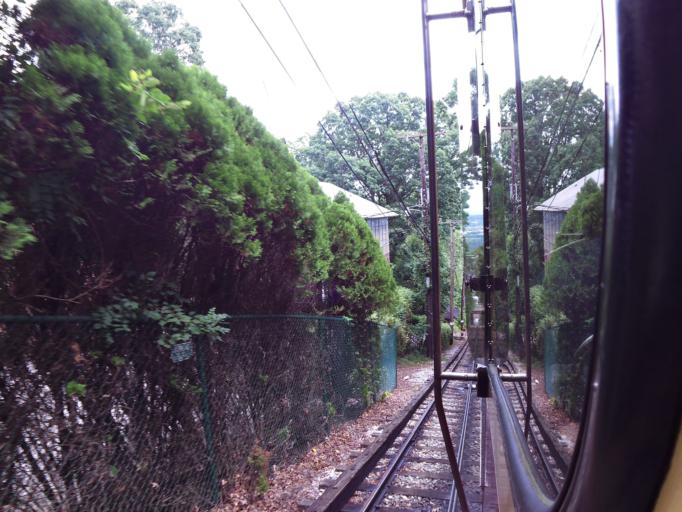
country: US
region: Tennessee
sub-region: Hamilton County
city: Lookout Mountain
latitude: 35.0070
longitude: -85.3395
